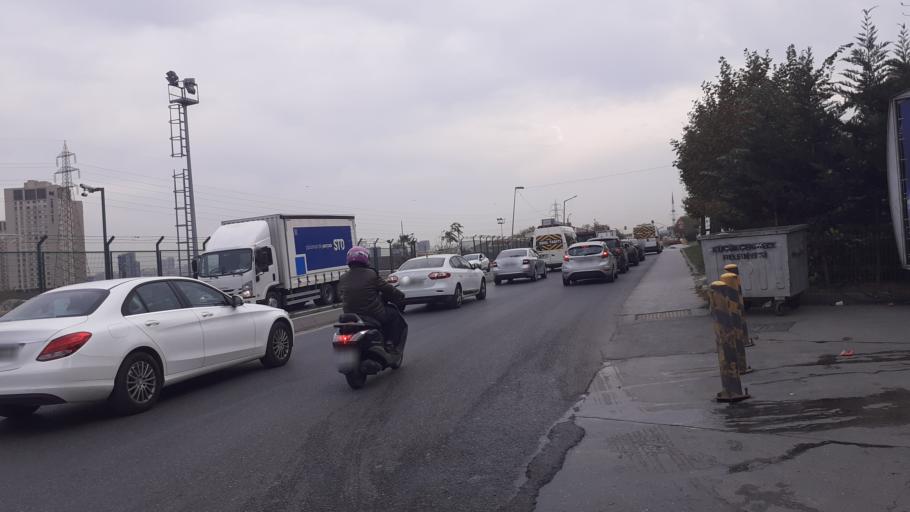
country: TR
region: Istanbul
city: Basaksehir
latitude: 41.0601
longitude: 28.7898
